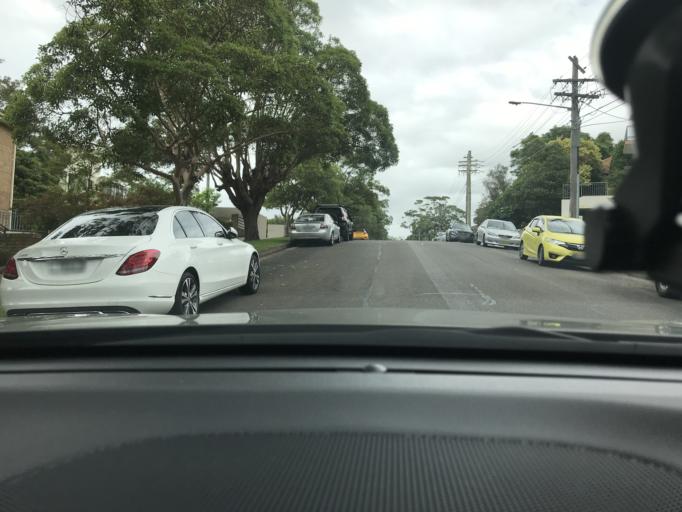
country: AU
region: New South Wales
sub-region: Canada Bay
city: Wareemba
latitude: -33.8465
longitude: 151.1311
